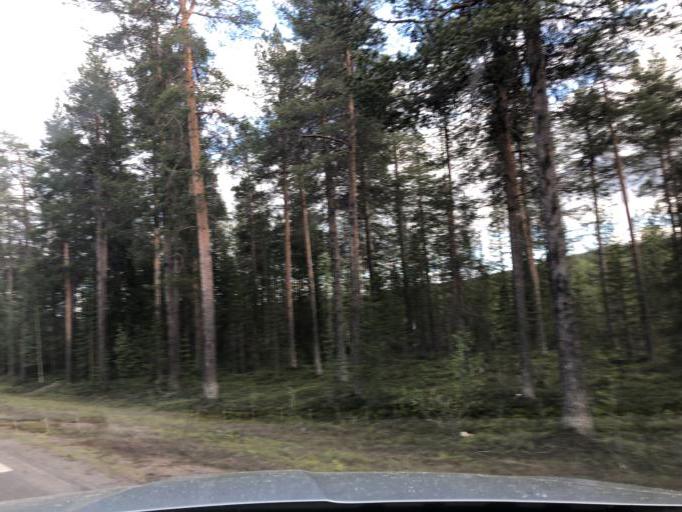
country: SE
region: Norrbotten
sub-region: Arvidsjaurs Kommun
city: Arvidsjaur
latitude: 65.6109
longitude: 19.0744
